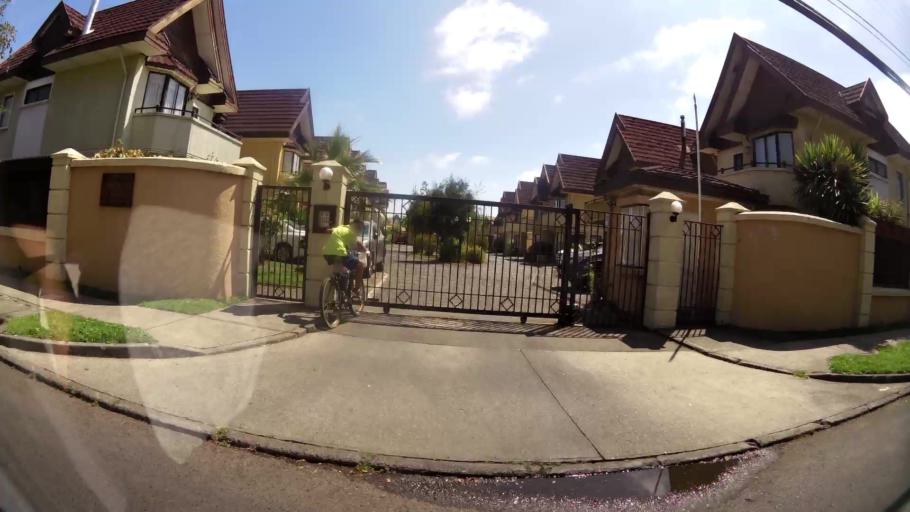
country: CL
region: Biobio
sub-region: Provincia de Concepcion
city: Concepcion
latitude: -36.7795
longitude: -73.0491
